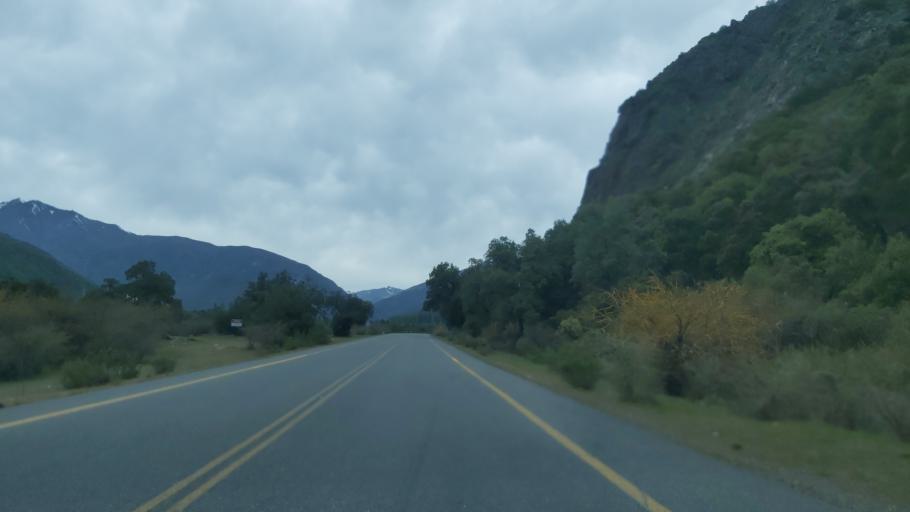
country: CL
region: Maule
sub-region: Provincia de Linares
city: Colbun
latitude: -35.8055
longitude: -70.8889
